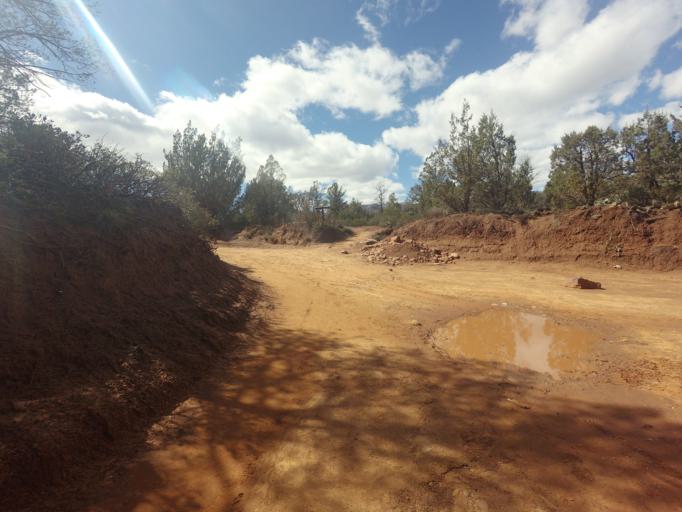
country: US
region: Arizona
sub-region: Yavapai County
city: West Sedona
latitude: 34.9030
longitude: -111.8141
